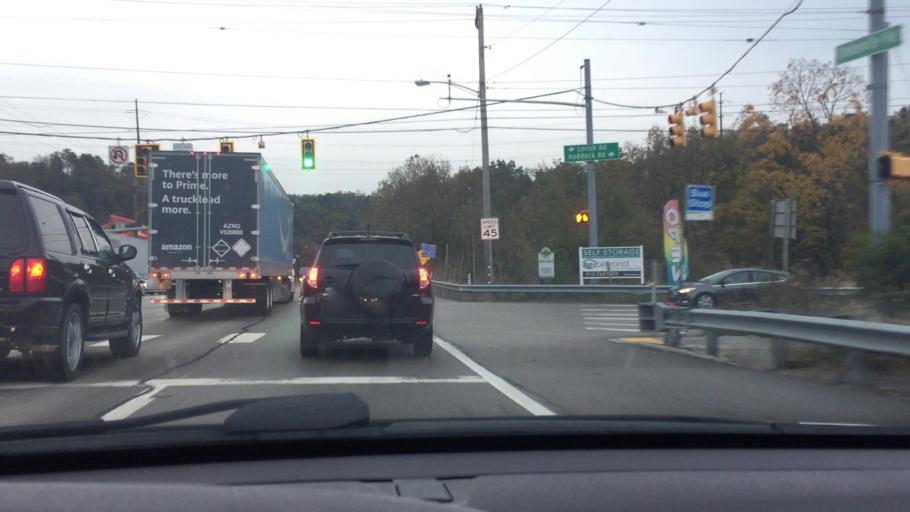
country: US
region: Pennsylvania
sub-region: Allegheny County
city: Ingram
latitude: 40.4495
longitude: -80.1078
